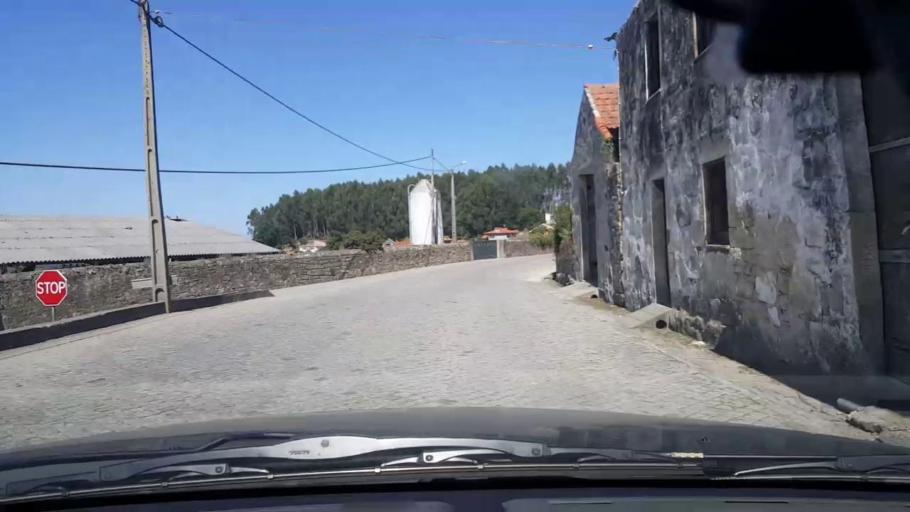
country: PT
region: Porto
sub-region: Maia
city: Gemunde
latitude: 41.3283
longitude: -8.6440
